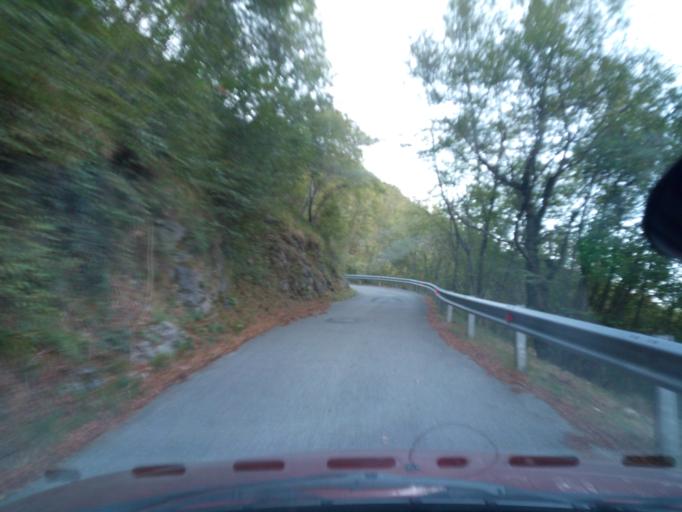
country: IT
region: Liguria
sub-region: Provincia di Genova
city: Isoverde
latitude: 44.4938
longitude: 8.8417
